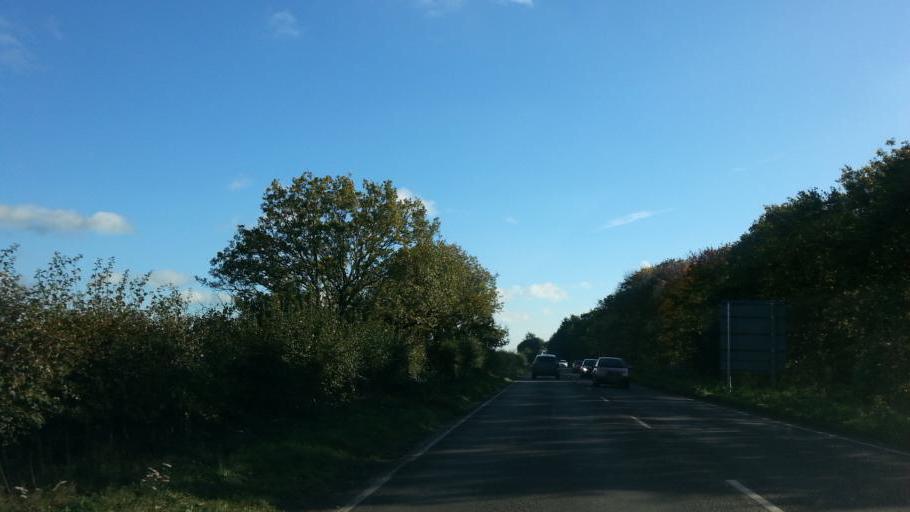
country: GB
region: England
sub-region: Suffolk
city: Beccles
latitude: 52.4823
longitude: 1.5283
